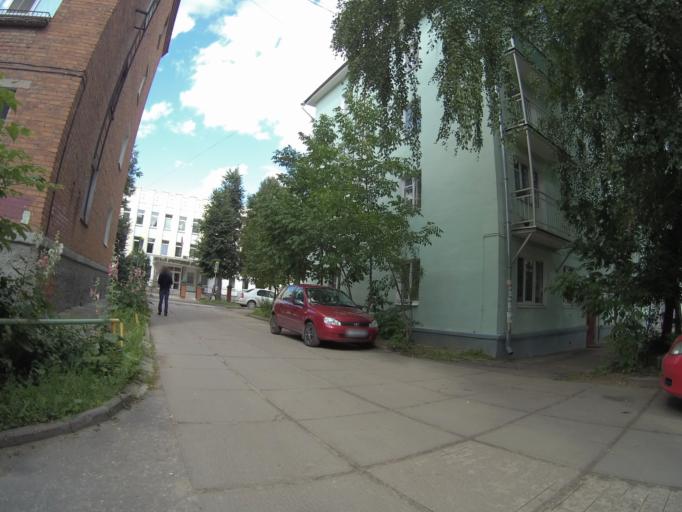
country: RU
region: Vladimir
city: Vladimir
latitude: 56.1406
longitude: 40.3979
